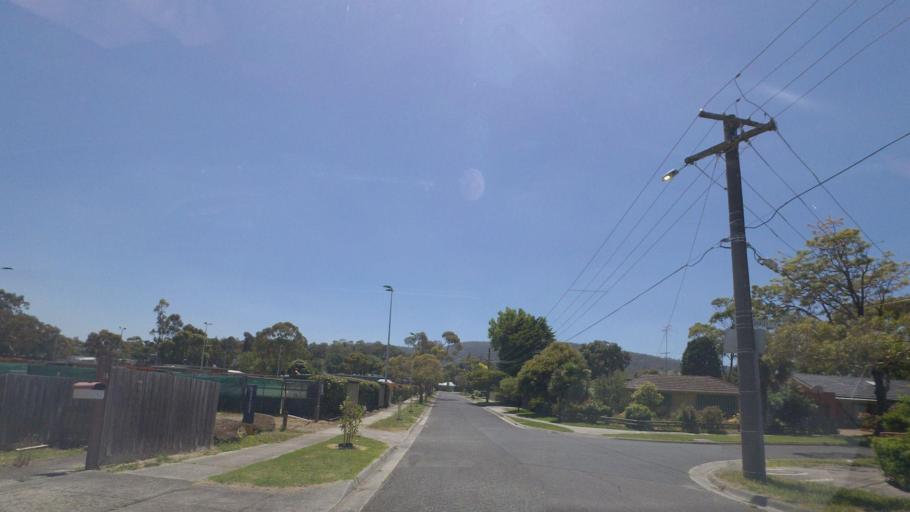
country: AU
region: Victoria
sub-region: Knox
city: Ferntree Gully
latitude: -37.8910
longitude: 145.2853
